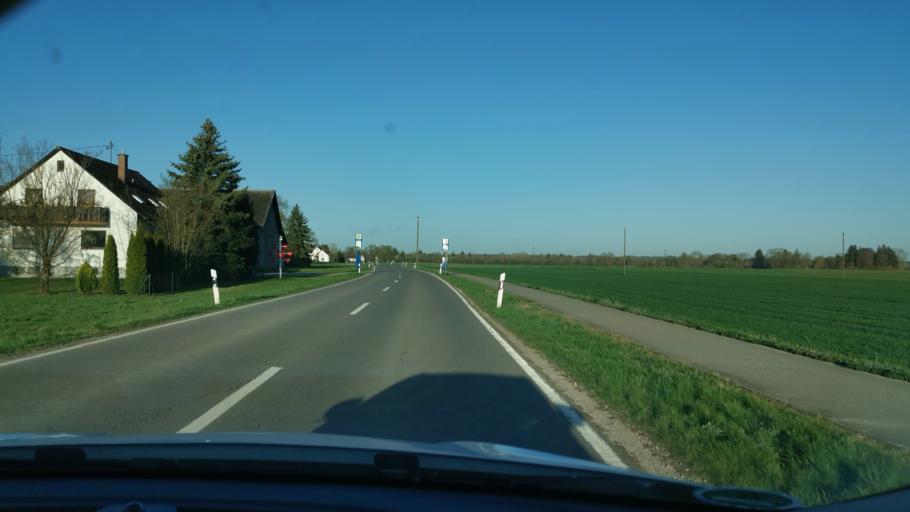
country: DE
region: Bavaria
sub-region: Swabia
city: Rehling
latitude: 48.4911
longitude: 10.9018
